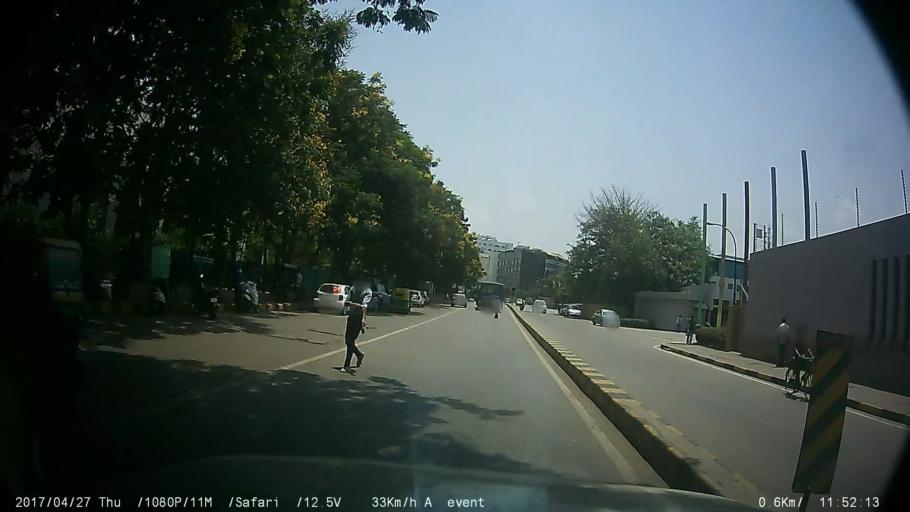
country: IN
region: Karnataka
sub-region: Bangalore Urban
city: Anekal
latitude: 12.8375
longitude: 77.6582
